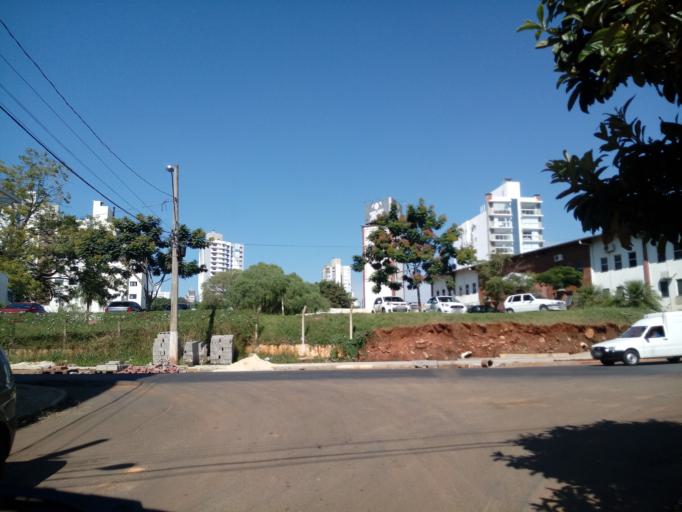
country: BR
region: Santa Catarina
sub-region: Chapeco
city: Chapeco
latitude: -27.0881
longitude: -52.6155
